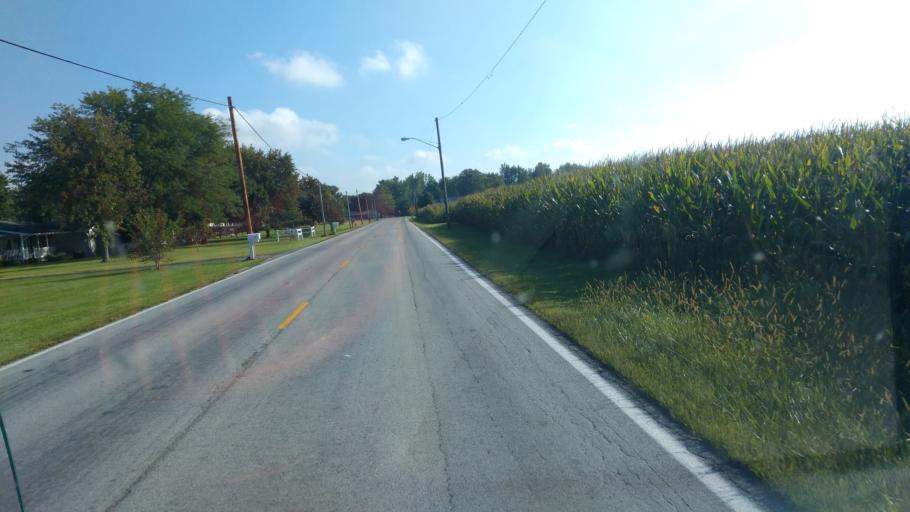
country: US
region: Ohio
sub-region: Hardin County
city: Forest
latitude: 40.8063
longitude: -83.5201
